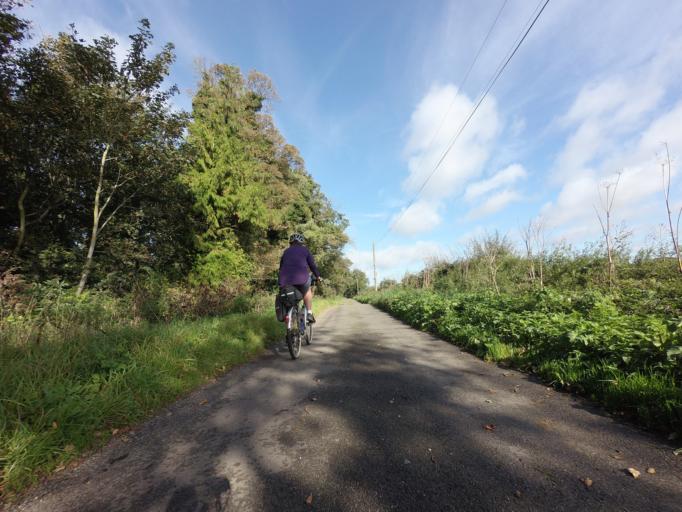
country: GB
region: England
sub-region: Norfolk
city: Fakenham
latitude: 52.8874
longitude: 0.6838
